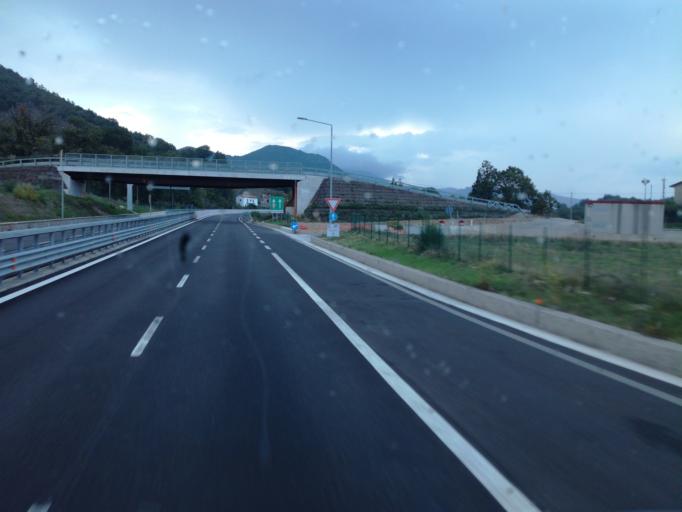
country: IT
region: Calabria
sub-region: Provincia di Cosenza
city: Laino Borgo
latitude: 39.9669
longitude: 15.9327
